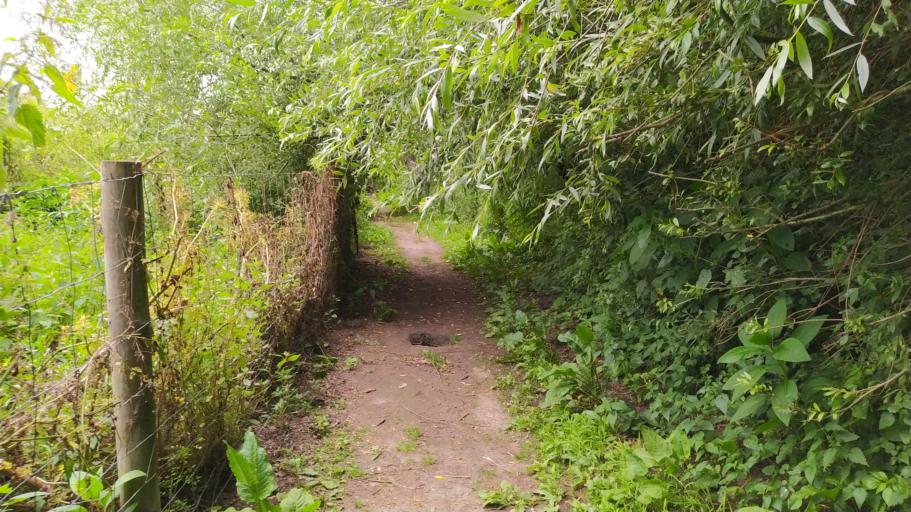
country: PT
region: Aveiro
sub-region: Aveiro
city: Aradas
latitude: 40.6233
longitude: -8.6468
